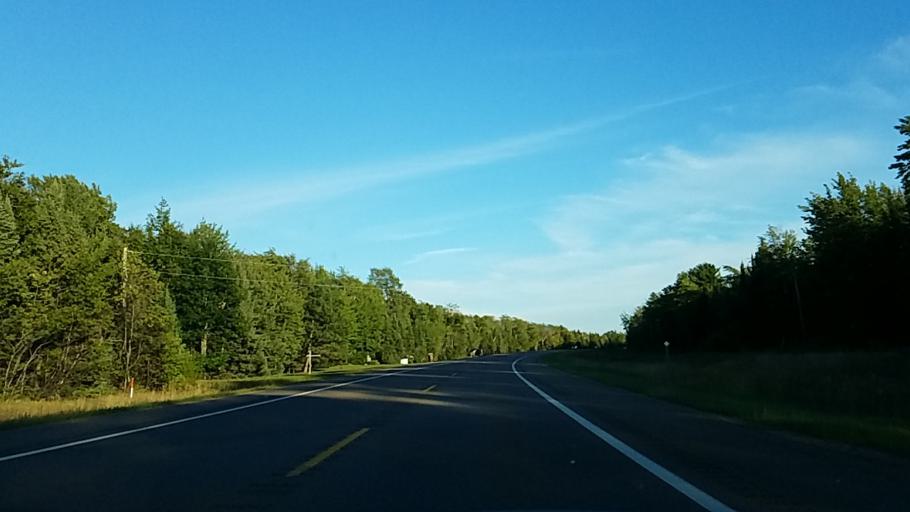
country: US
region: Michigan
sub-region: Alger County
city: Munising
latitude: 46.4610
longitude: -86.8965
